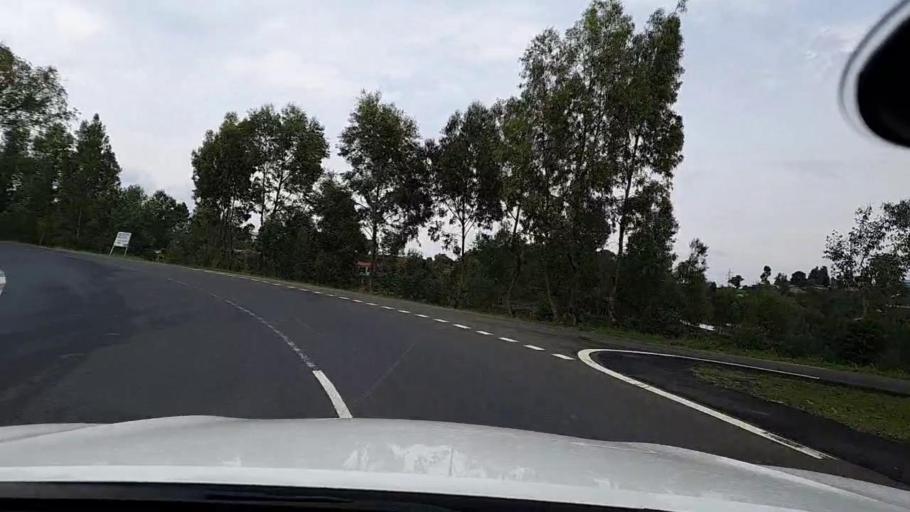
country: RW
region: Western Province
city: Kibuye
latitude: -2.1552
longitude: 29.2969
